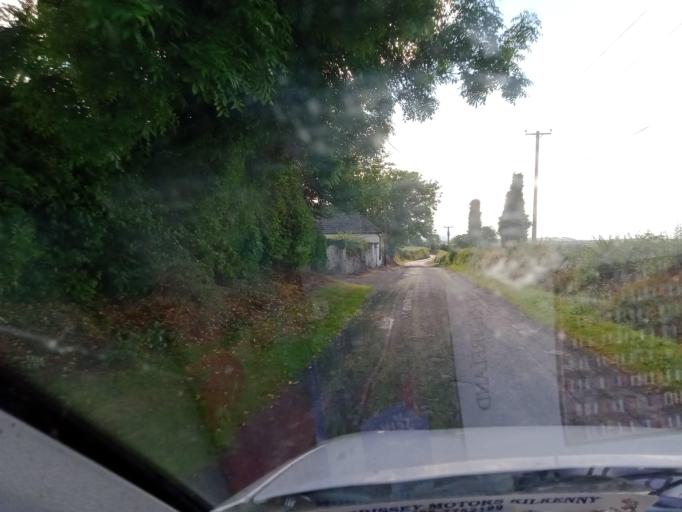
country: IE
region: Leinster
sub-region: Laois
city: Rathdowney
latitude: 52.7729
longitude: -7.5088
